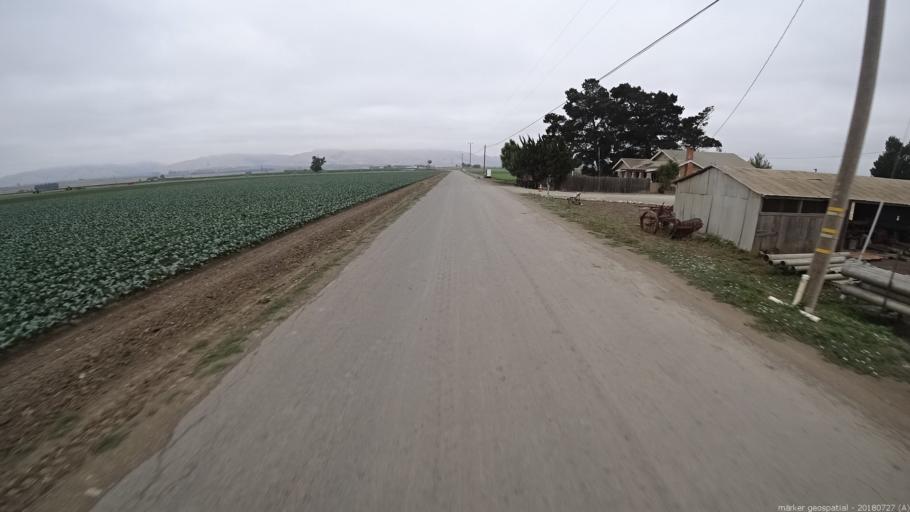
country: US
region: California
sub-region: Monterey County
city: Greenfield
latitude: 36.3158
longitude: -121.2166
